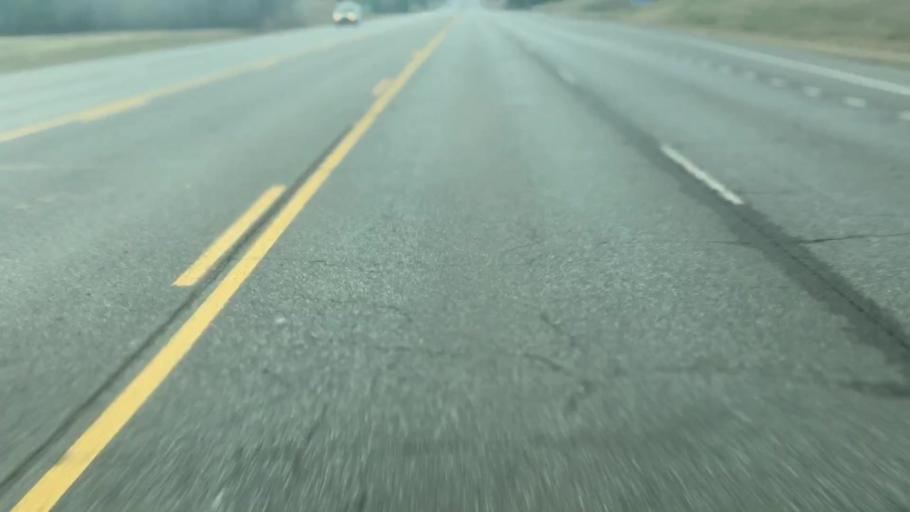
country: US
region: Alabama
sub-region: Walker County
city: Jasper
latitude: 33.8094
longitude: -87.2342
